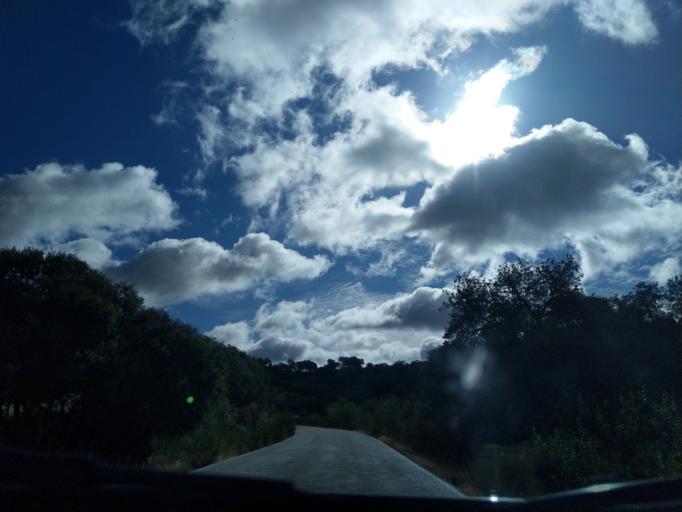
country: ES
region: Extremadura
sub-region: Provincia de Badajoz
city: Reina
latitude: 38.1323
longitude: -5.9176
